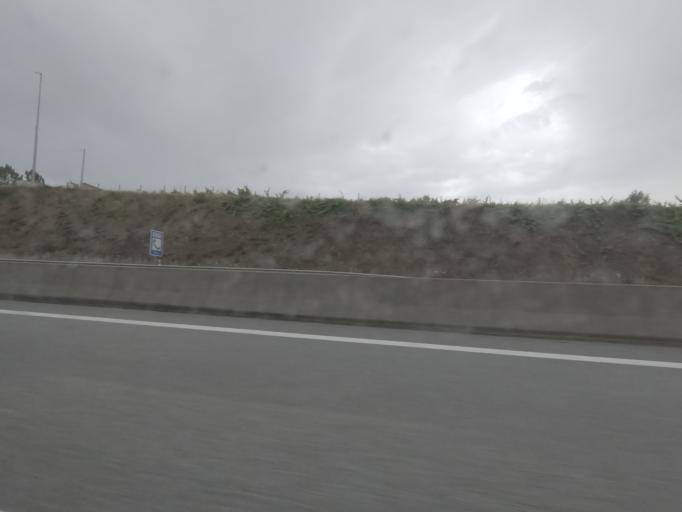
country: PT
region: Vila Real
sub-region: Vila Real
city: Vila Real
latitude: 41.2848
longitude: -7.7046
